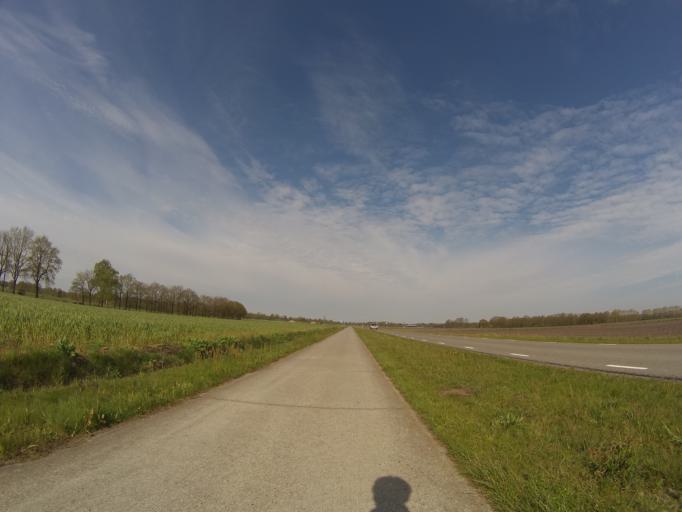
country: NL
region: Drenthe
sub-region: Gemeente Coevorden
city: Sleen
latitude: 52.7939
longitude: 6.7514
